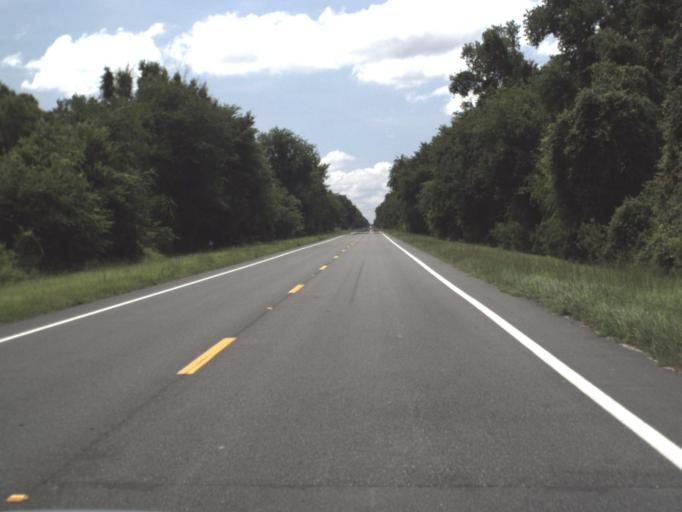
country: US
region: Florida
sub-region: Hamilton County
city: Jasper
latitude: 30.4286
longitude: -82.8642
